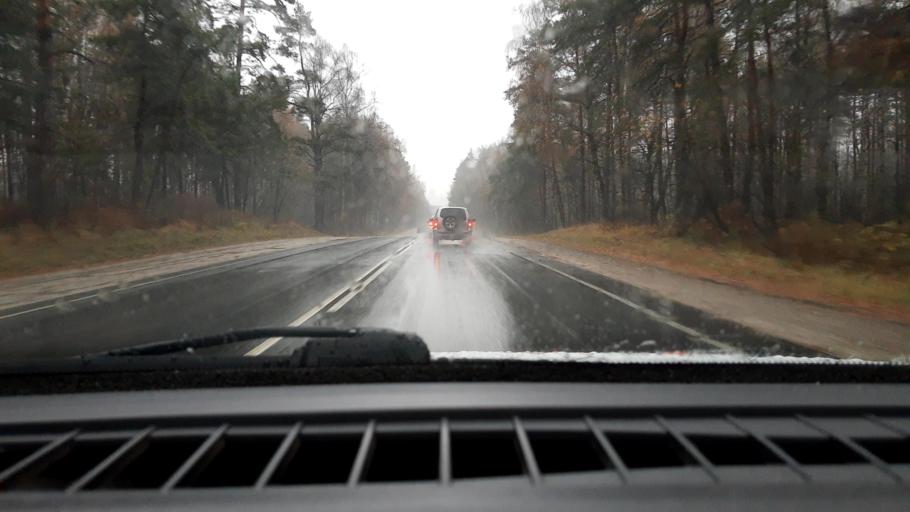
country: RU
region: Nizjnij Novgorod
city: Neklyudovo
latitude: 56.4379
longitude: 43.9981
